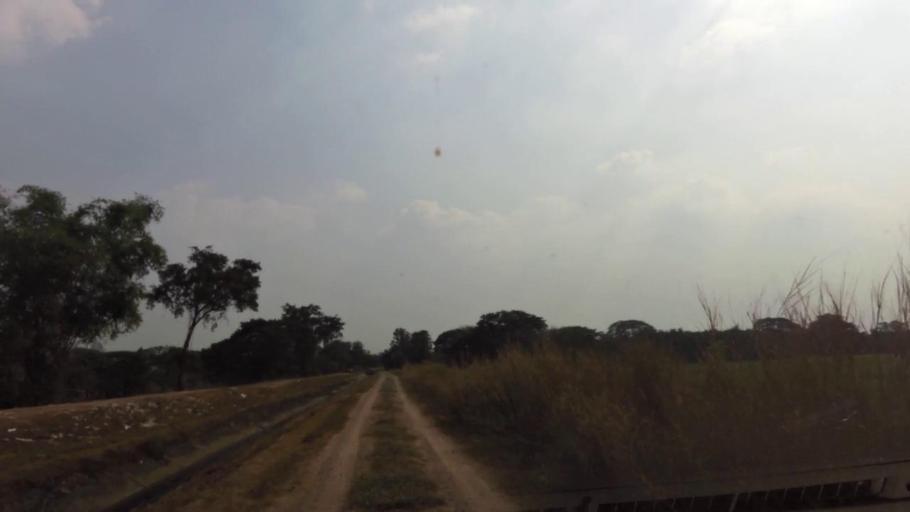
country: TH
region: Phra Nakhon Si Ayutthaya
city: Phra Nakhon Si Ayutthaya
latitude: 14.3125
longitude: 100.5625
